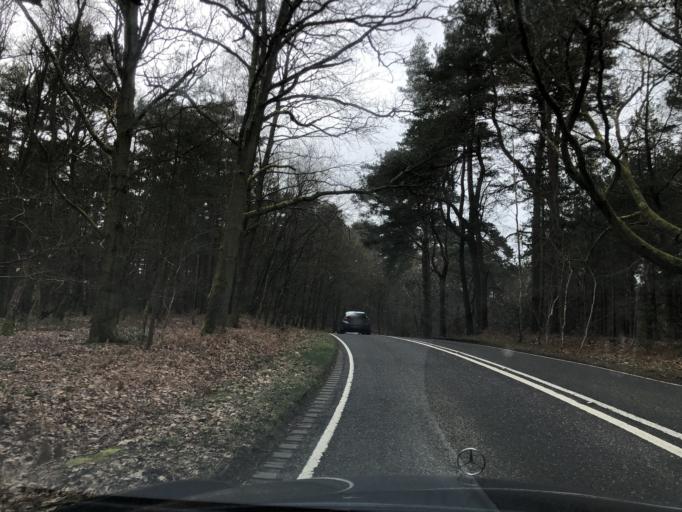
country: GB
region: England
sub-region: Surrey
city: Normandy
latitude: 51.2975
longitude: -0.6902
